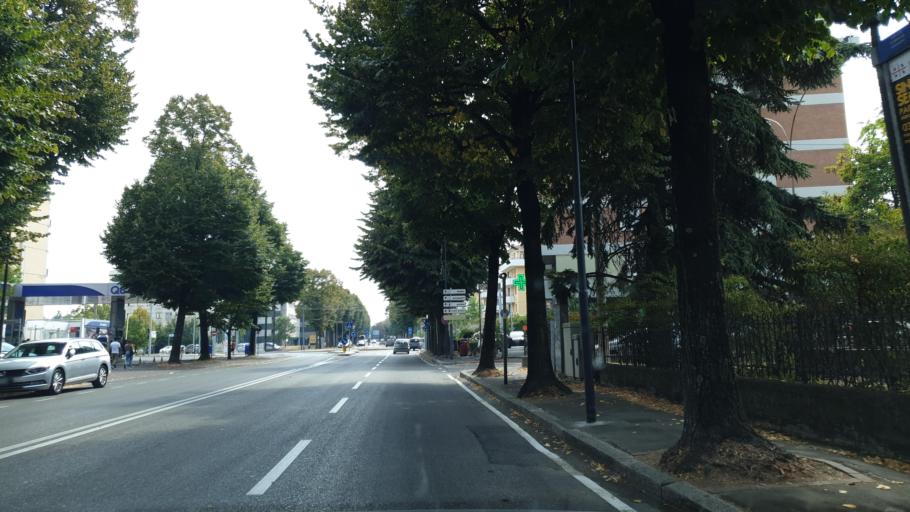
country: IT
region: Emilia-Romagna
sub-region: Provincia di Parma
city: Parma
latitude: 44.8005
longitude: 10.3044
